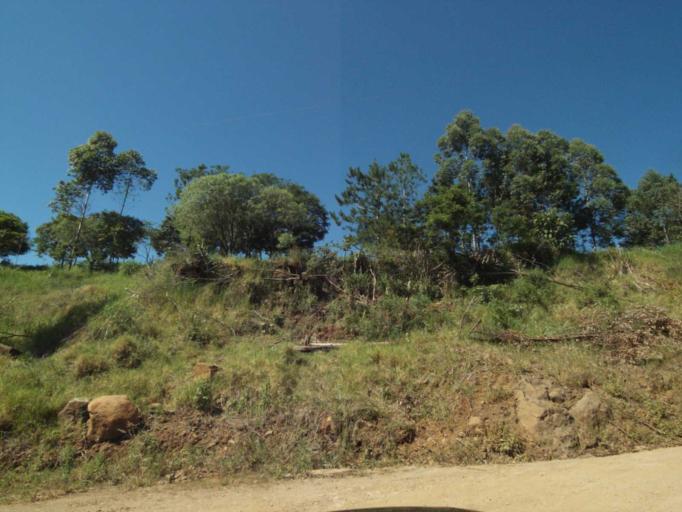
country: BR
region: Parana
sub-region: Francisco Beltrao
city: Francisco Beltrao
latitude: -26.1497
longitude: -53.3037
